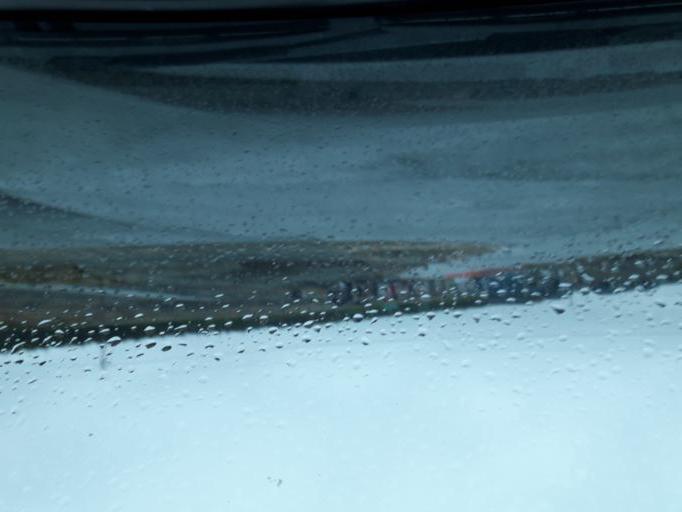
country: CA
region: Newfoundland and Labrador
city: Mount Pearl
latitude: 47.5586
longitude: -52.8042
